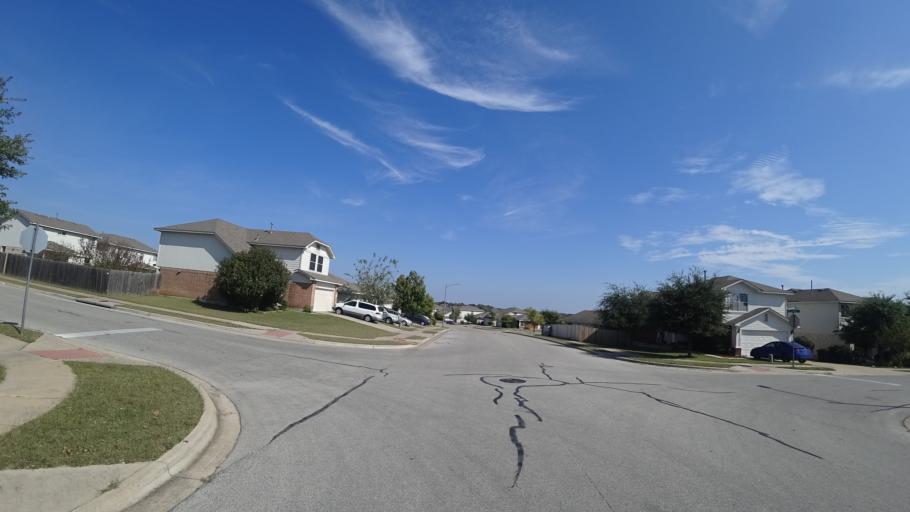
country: US
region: Texas
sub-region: Travis County
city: Pflugerville
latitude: 30.4261
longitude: -97.6375
